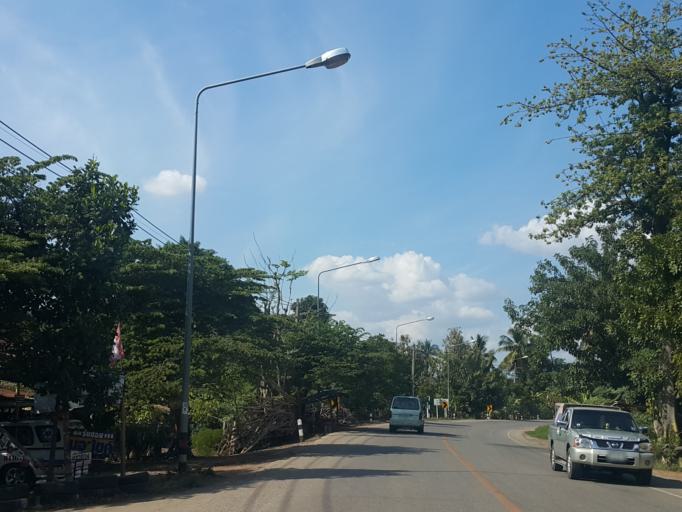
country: TH
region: Sukhothai
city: Sawankhalok
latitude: 17.2954
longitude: 99.8275
